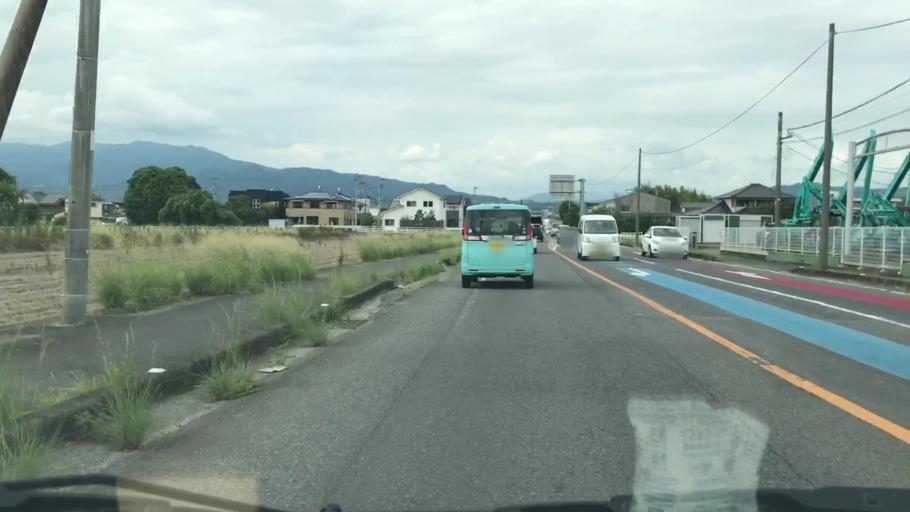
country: JP
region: Saga Prefecture
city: Saga-shi
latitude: 33.2692
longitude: 130.2615
